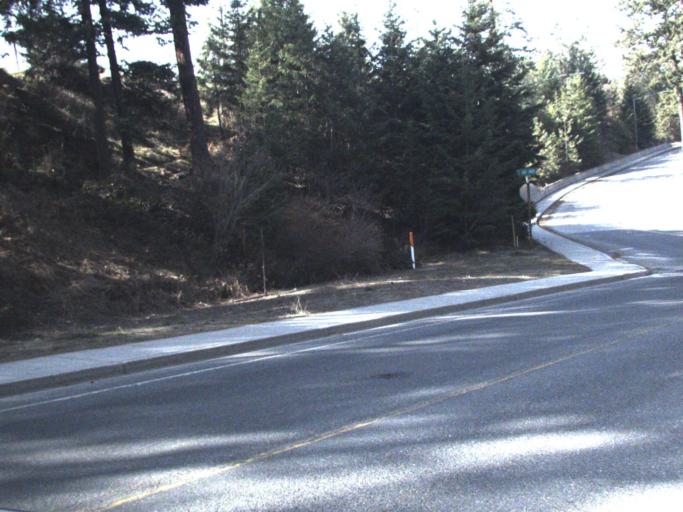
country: US
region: Washington
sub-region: Stevens County
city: Colville
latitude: 48.5469
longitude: -117.8855
